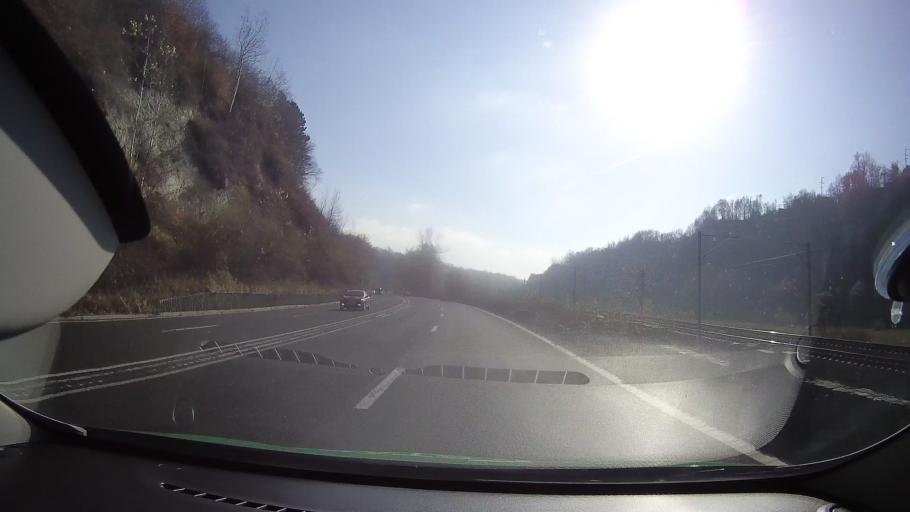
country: RO
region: Prahova
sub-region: Oras Breaza
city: Breaza de Jos
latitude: 45.1791
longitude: 25.6819
